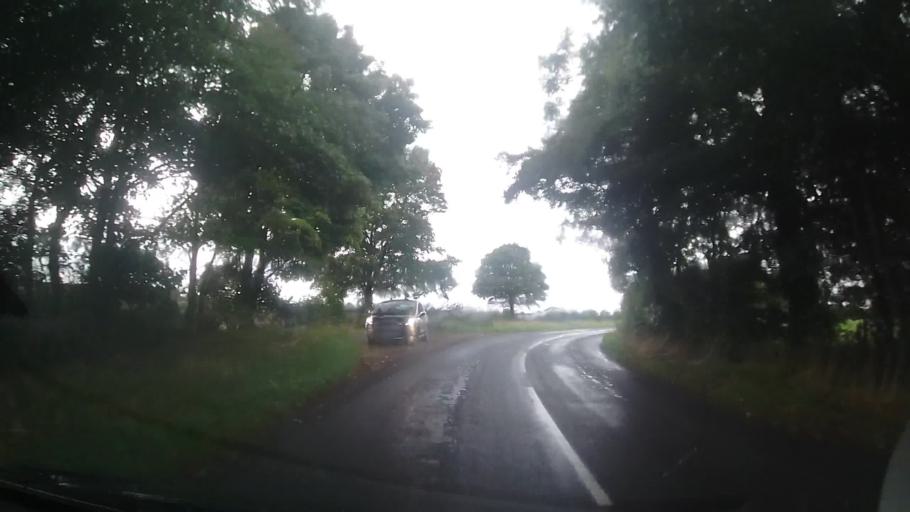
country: GB
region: England
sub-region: Oxfordshire
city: Stonesfield
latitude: 51.8694
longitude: -1.3939
